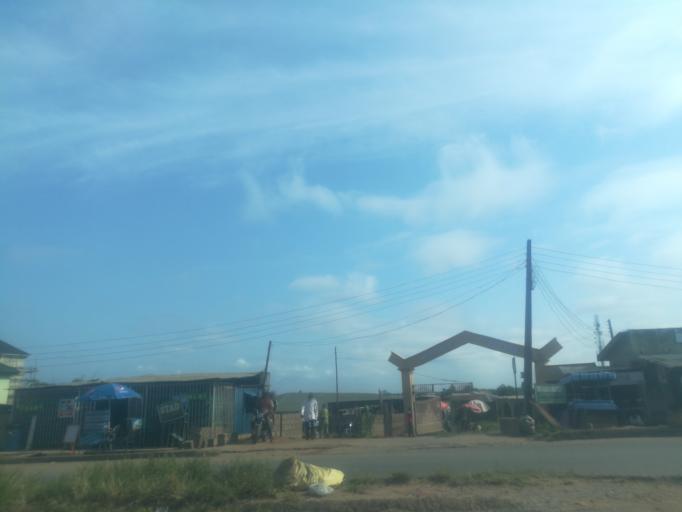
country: NG
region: Oyo
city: Ibadan
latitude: 7.3467
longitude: 3.8466
